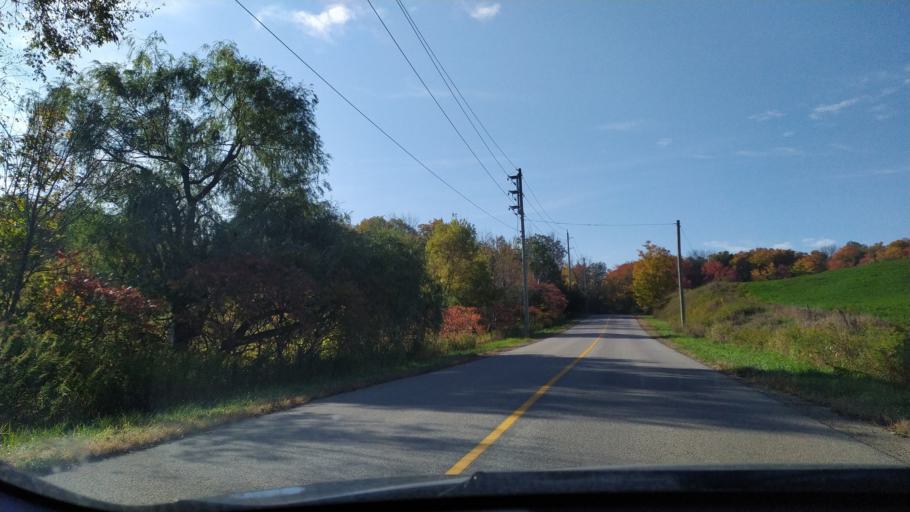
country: CA
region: Ontario
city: Waterloo
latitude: 43.4883
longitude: -80.6578
